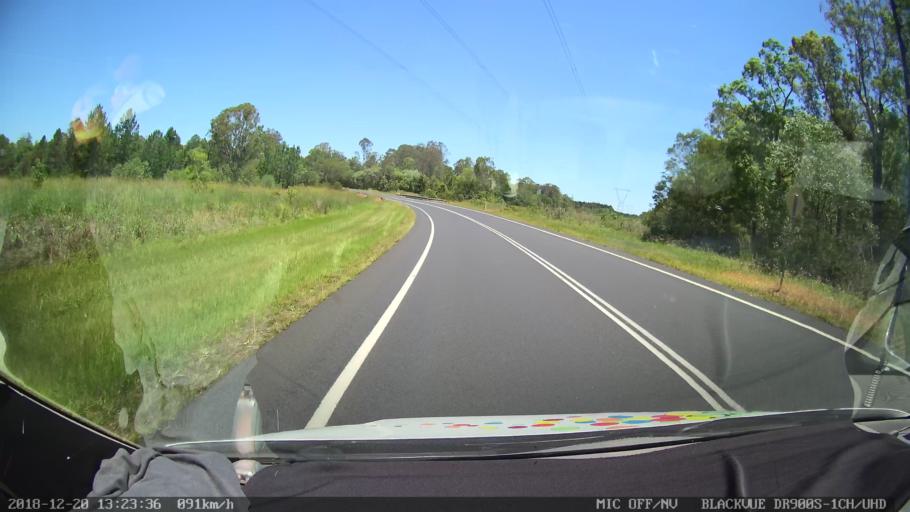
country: AU
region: New South Wales
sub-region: Richmond Valley
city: Casino
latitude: -29.1067
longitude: 152.9989
